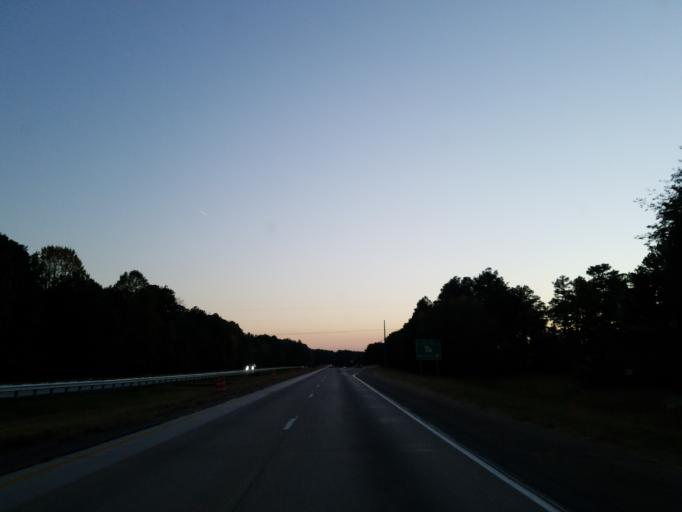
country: US
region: Georgia
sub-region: Forsyth County
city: Cumming
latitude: 34.1625
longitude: -84.1667
